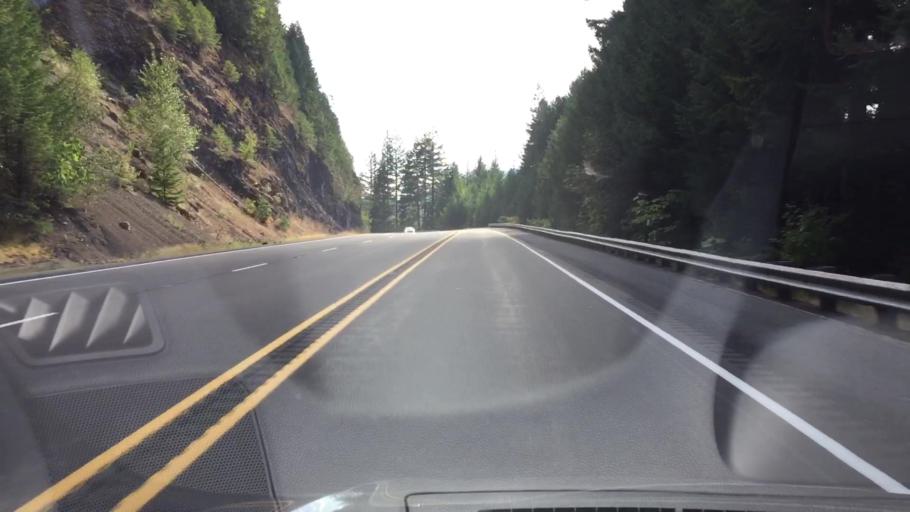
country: US
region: Washington
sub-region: Pierce County
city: Buckley
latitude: 46.6686
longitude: -121.5925
